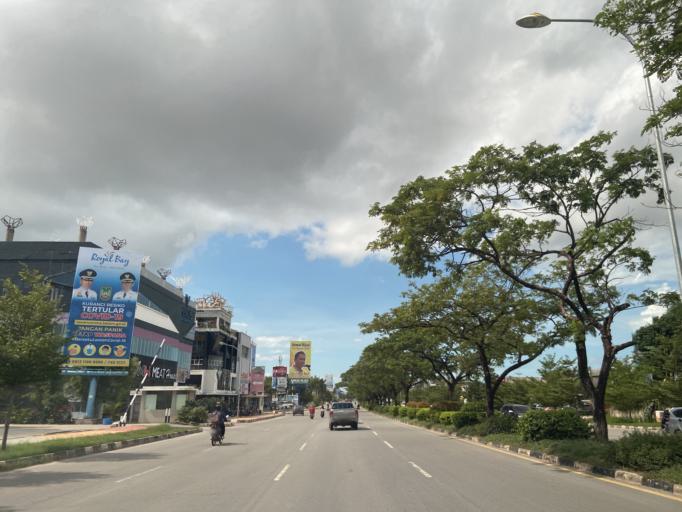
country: SG
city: Singapore
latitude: 1.1318
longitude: 104.0404
